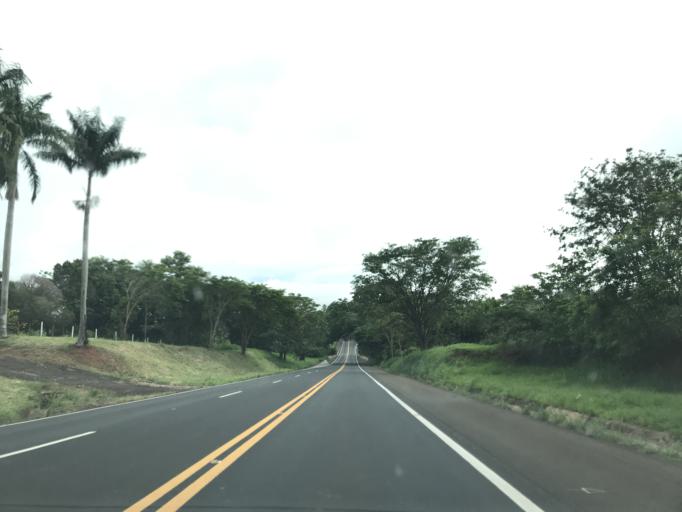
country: BR
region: Sao Paulo
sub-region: Penapolis
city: Penapolis
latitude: -21.4603
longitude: -50.1738
